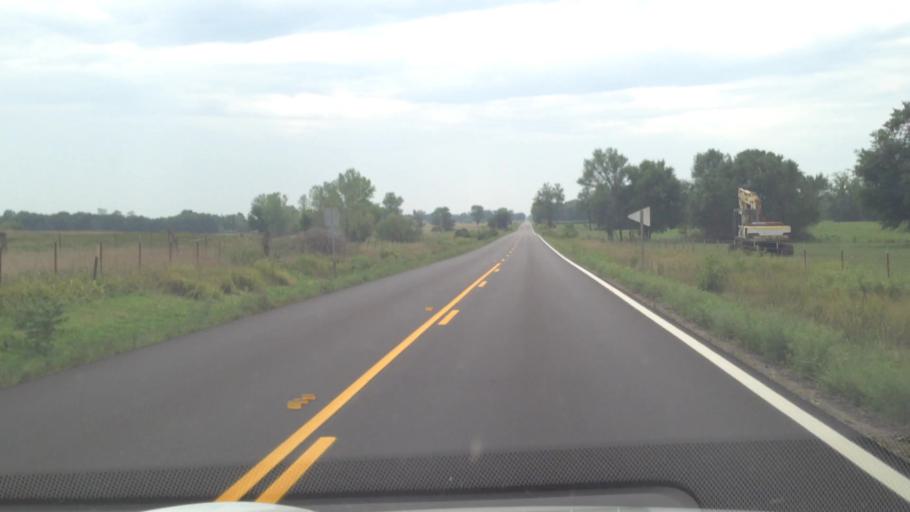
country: US
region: Kansas
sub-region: Crawford County
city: Girard
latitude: 37.5430
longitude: -94.9605
